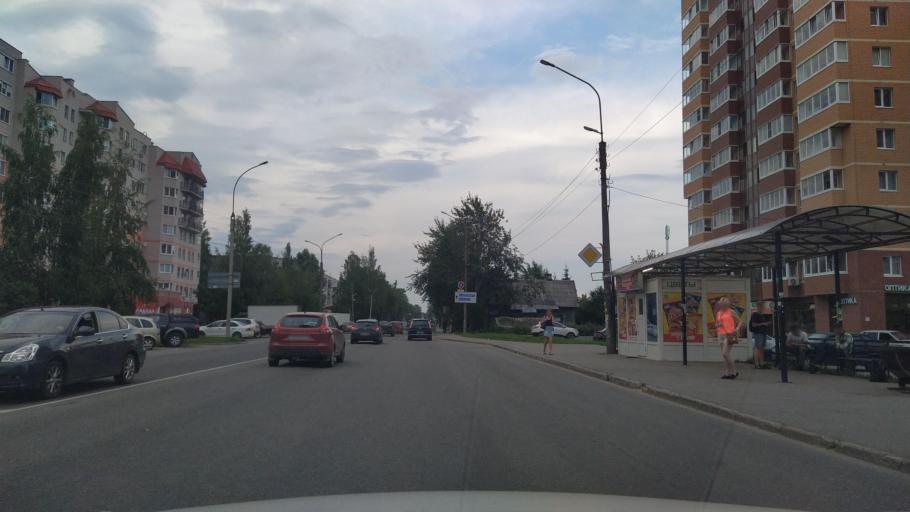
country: RU
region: Novgorod
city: Velikiy Novgorod
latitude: 58.5164
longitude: 31.2466
